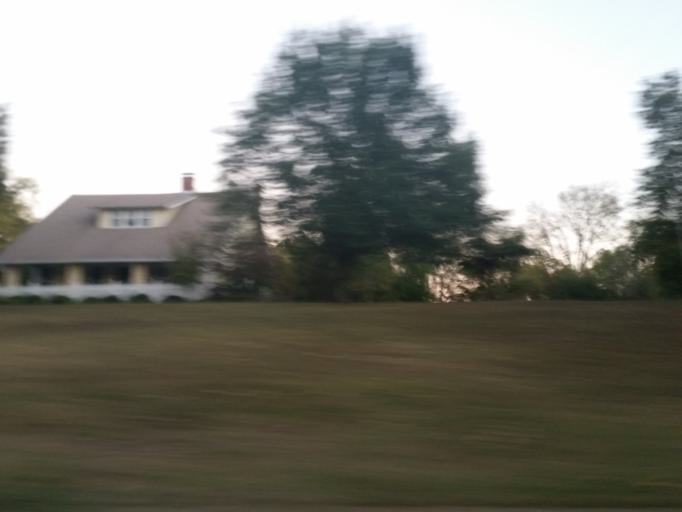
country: US
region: Tennessee
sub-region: Knox County
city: Knoxville
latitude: 36.0424
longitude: -83.9076
